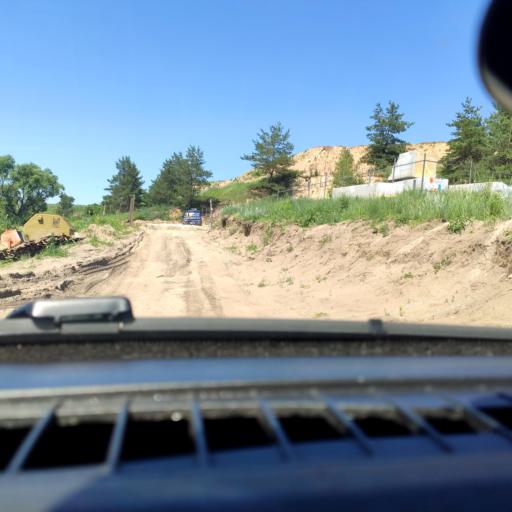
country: RU
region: Voronezj
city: Podgornoye
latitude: 51.7977
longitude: 39.1359
